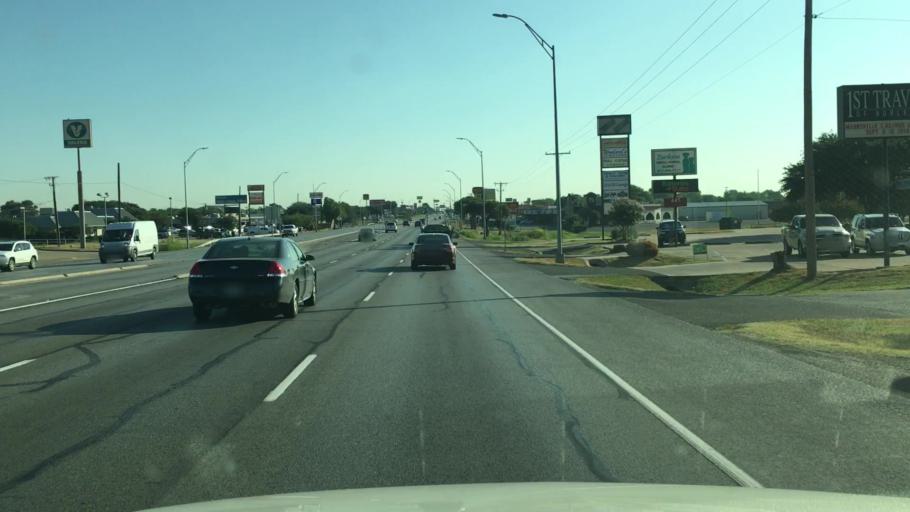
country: US
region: Texas
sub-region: Johnson County
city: Burleson
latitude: 32.5378
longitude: -97.3334
